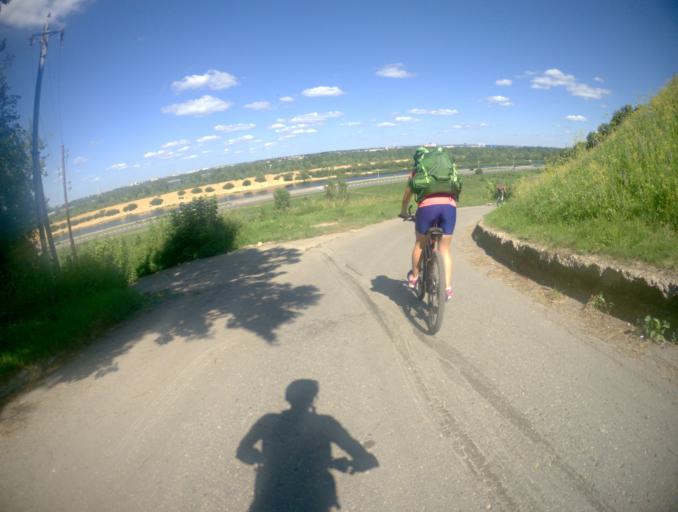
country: RU
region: Nizjnij Novgorod
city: Bor
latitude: 56.3241
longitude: 44.0475
